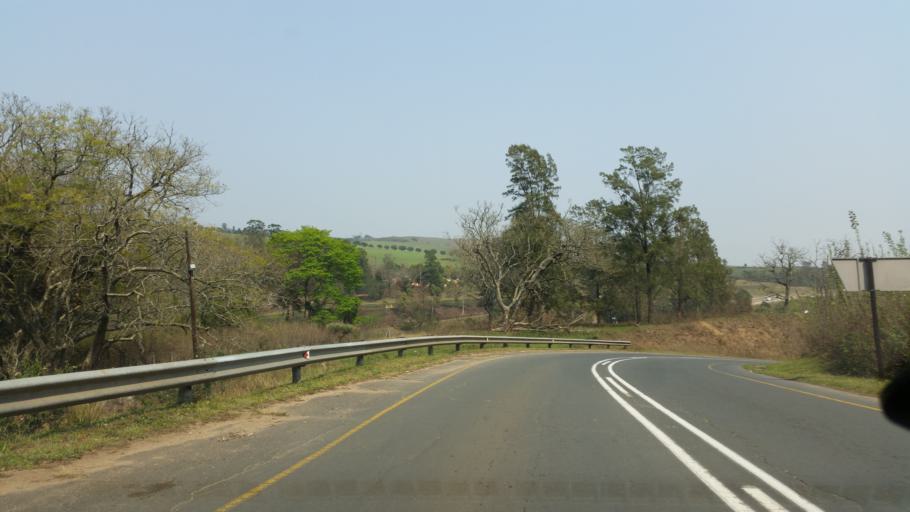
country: ZA
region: KwaZulu-Natal
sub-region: eThekwini Metropolitan Municipality
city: Mpumalanga
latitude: -29.7403
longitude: 30.6628
